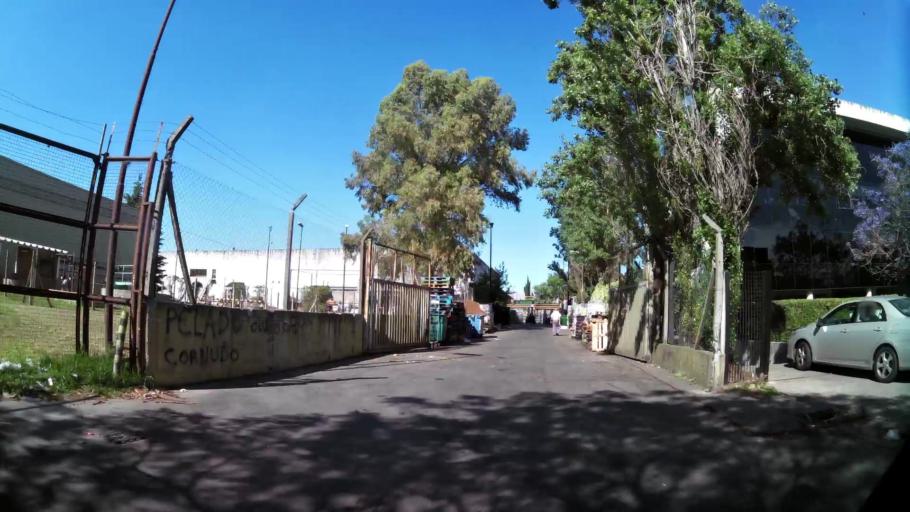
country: AR
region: Buenos Aires
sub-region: Partido de Tigre
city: Tigre
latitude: -34.4754
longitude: -58.5734
